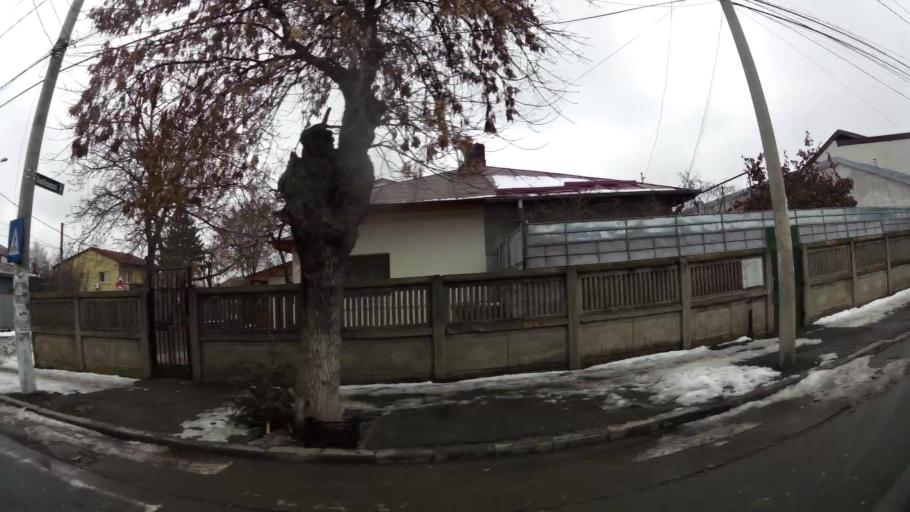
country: RO
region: Ilfov
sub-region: Comuna Chiajna
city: Rosu
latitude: 44.4809
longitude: 26.0263
